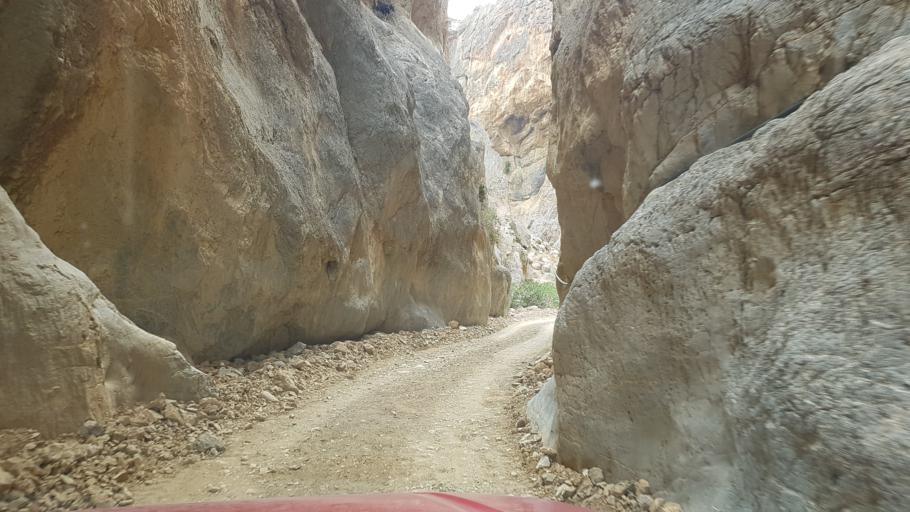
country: GR
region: Crete
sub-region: Nomos Irakleiou
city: Agioi Deka
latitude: 34.9429
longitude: 24.9849
